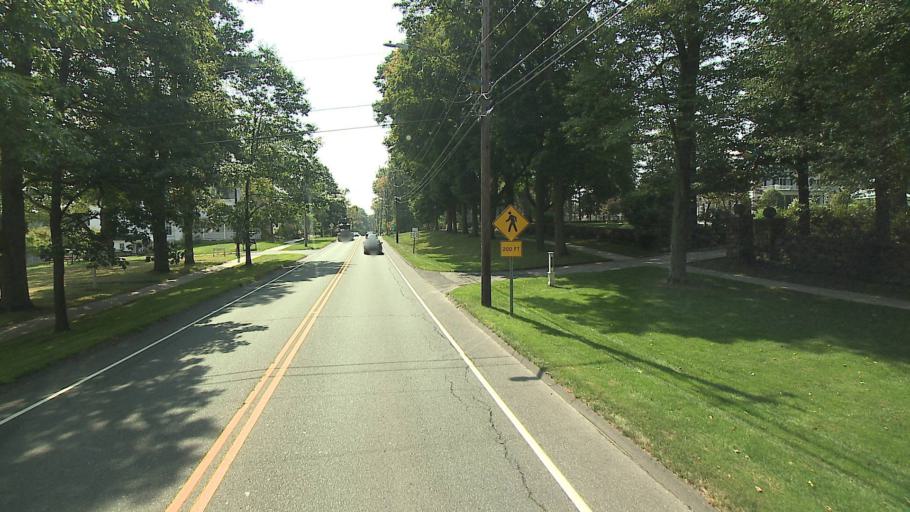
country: US
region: Connecticut
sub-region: Fairfield County
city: Ridgefield
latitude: 41.2775
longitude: -73.4979
